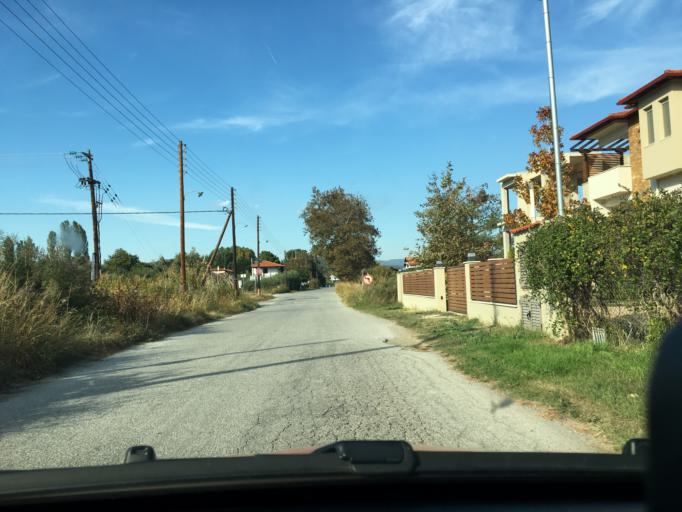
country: GR
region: Central Macedonia
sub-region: Nomos Chalkidikis
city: Agios Nikolaos
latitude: 40.2930
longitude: 23.6937
